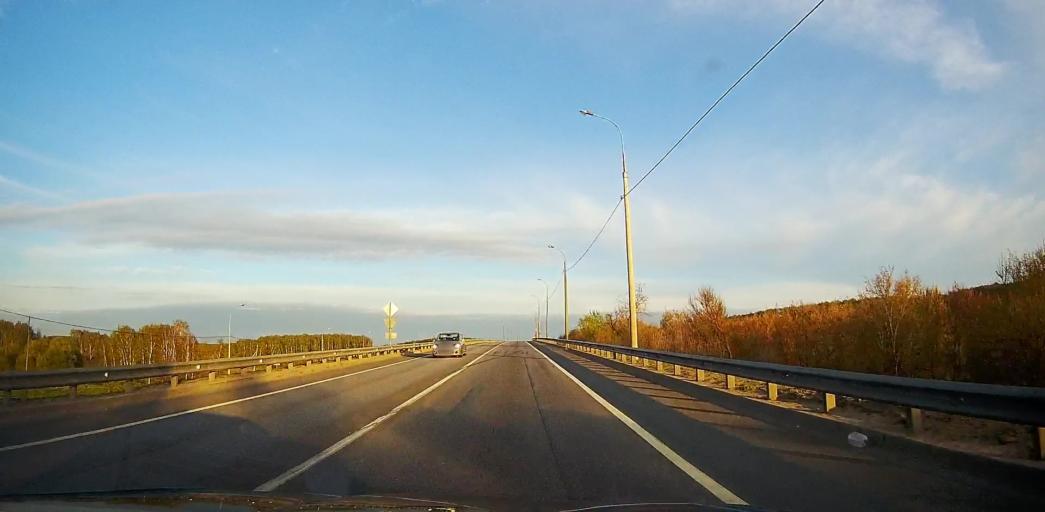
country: RU
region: Moskovskaya
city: Troitskoye
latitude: 55.2385
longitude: 38.5426
